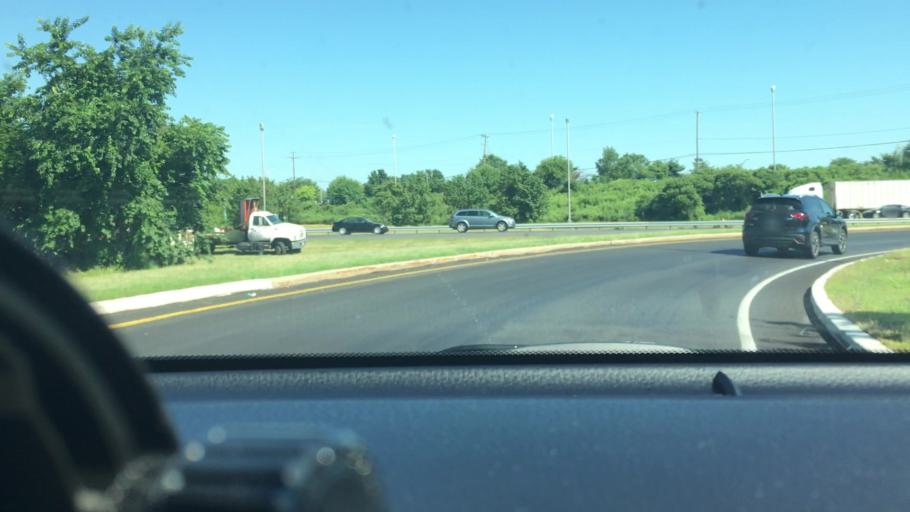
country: US
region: New Jersey
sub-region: Burlington County
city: Mount Laurel
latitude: 39.9684
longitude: -74.9110
